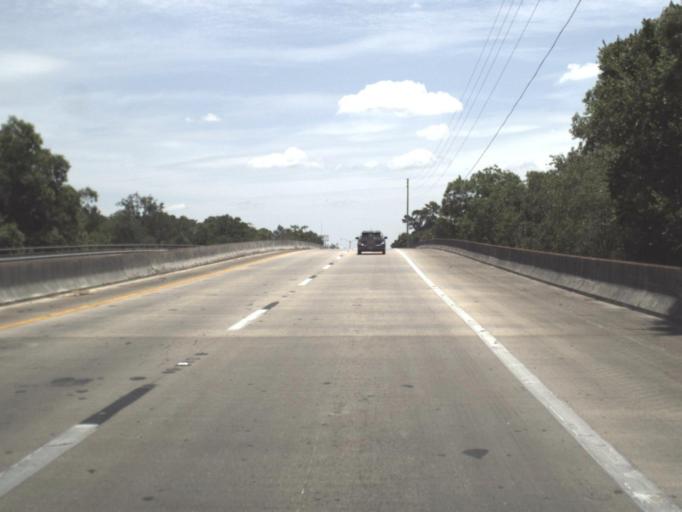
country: US
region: Florida
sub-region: Levy County
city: Manatee Road
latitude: 29.5912
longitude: -82.9390
